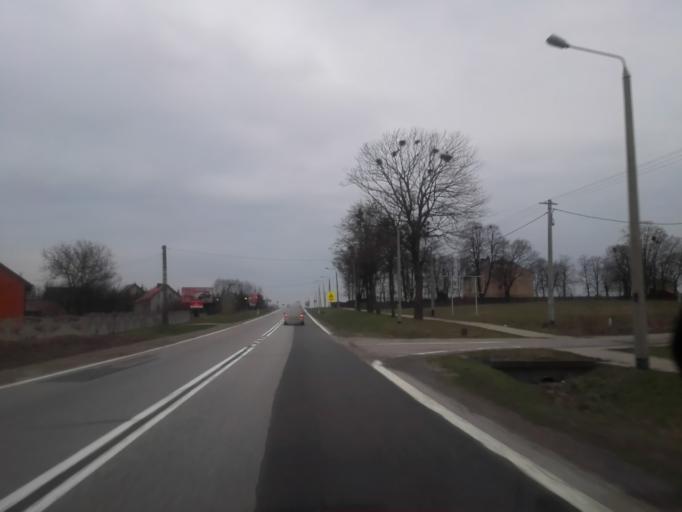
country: PL
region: Podlasie
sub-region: Powiat lomzynski
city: Piatnica
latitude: 53.2486
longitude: 22.1195
